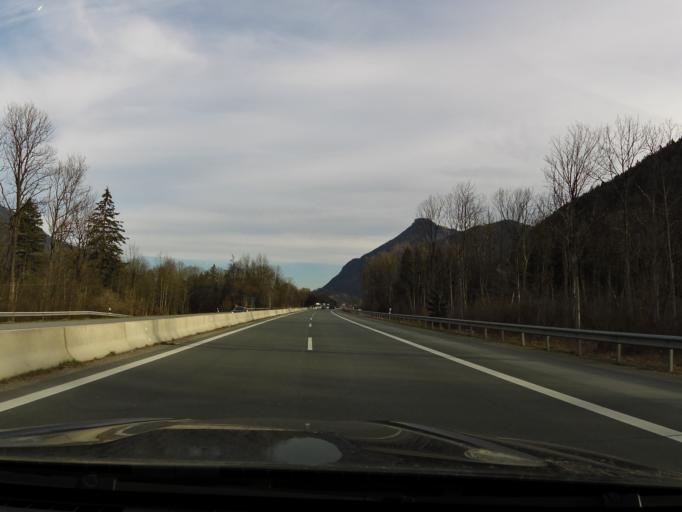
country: DE
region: Bavaria
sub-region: Upper Bavaria
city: Oberaudorf
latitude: 47.6568
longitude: 12.1846
